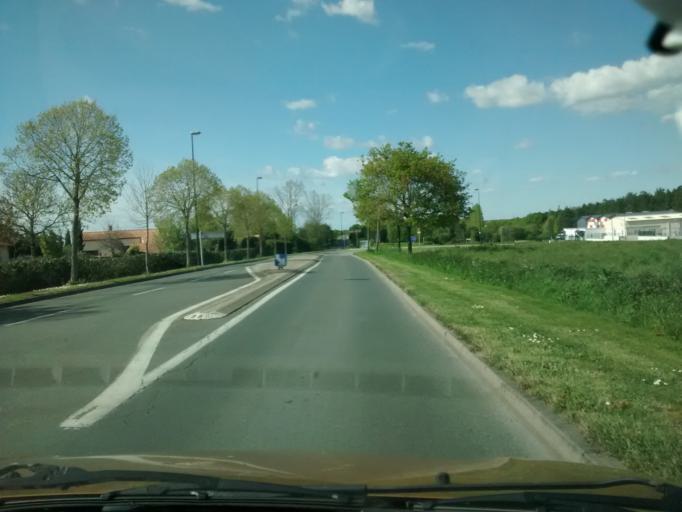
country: FR
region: Pays de la Loire
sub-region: Departement de la Vendee
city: Les Lucs-sur-Boulogne
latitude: 46.8486
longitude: -1.4947
